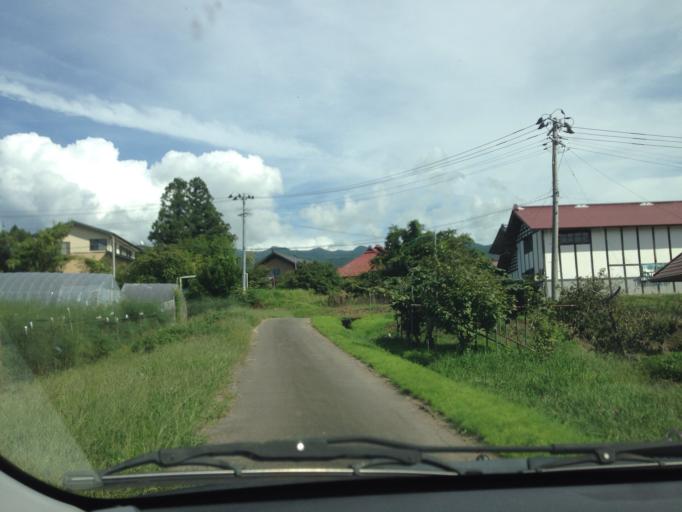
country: JP
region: Fukushima
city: Kitakata
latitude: 37.6177
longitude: 139.9324
